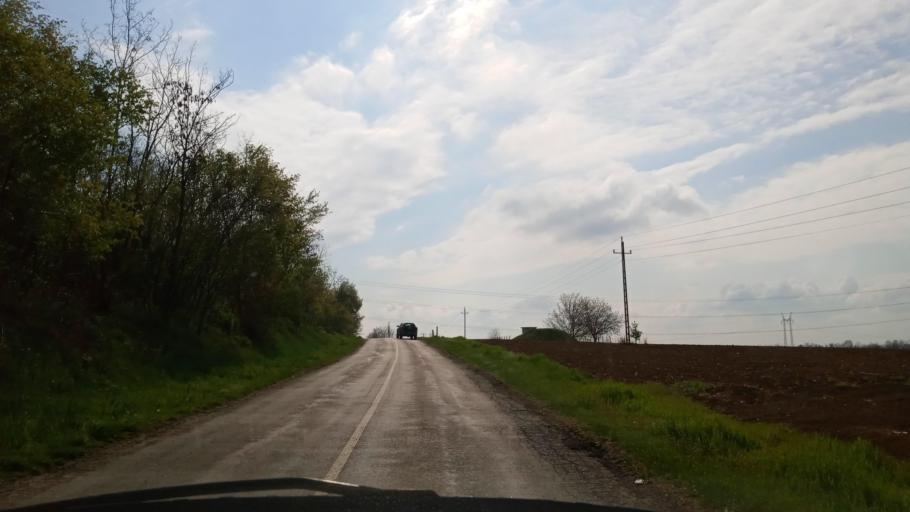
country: HU
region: Baranya
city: Pecsvarad
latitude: 46.1544
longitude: 18.4383
